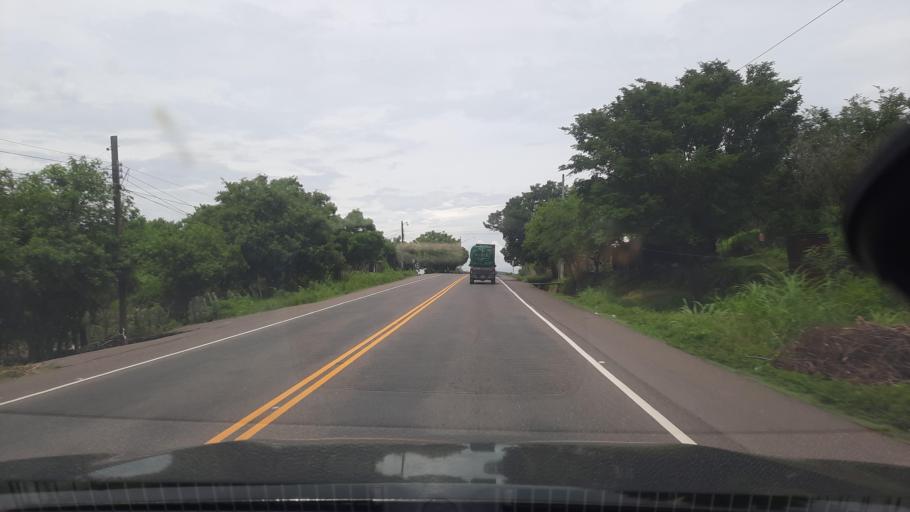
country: HN
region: Valle
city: Goascoran
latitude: 13.5479
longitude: -87.6393
